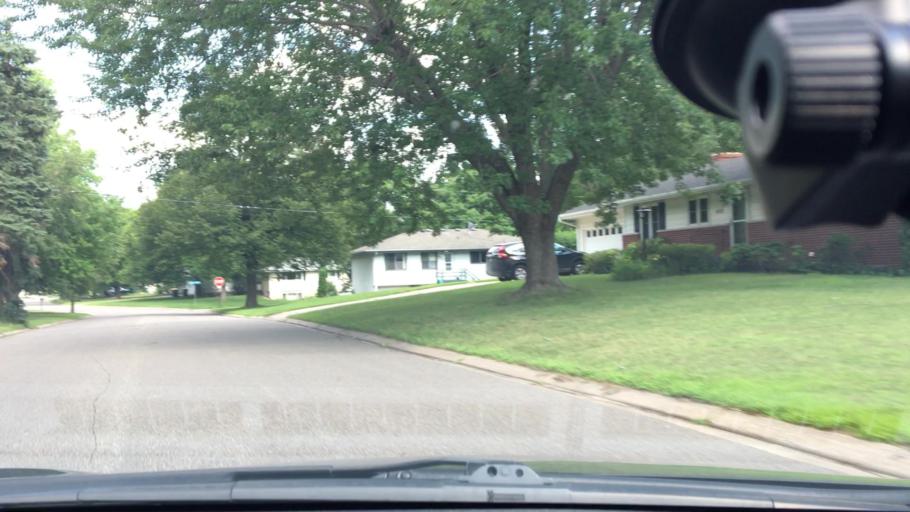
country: US
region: Minnesota
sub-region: Hennepin County
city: New Hope
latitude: 45.0376
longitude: -93.3903
